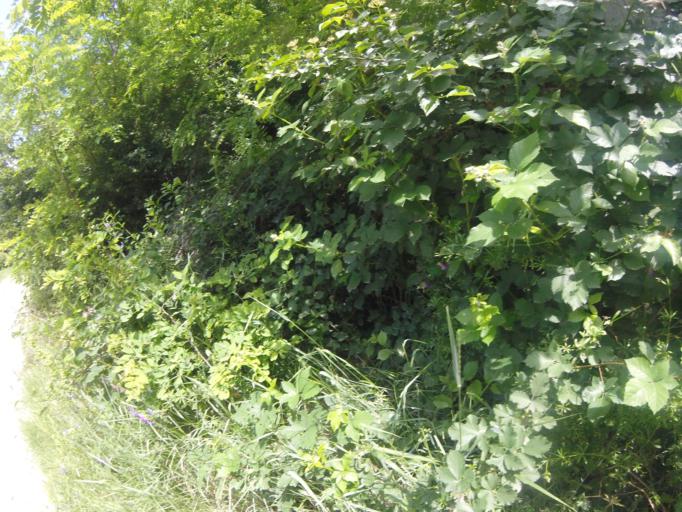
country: HU
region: Zala
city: Zalaszentgrot
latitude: 46.8844
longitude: 17.0346
